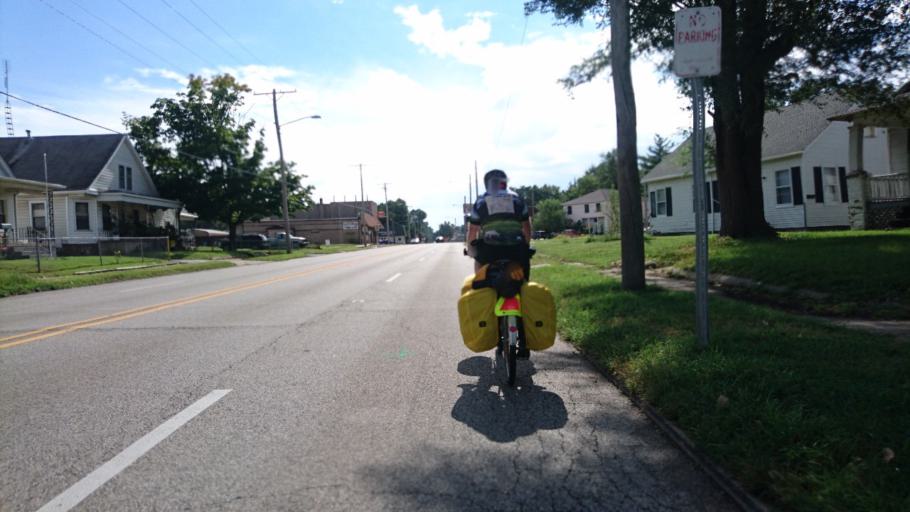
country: US
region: Illinois
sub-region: Sangamon County
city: Grandview
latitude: 39.8280
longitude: -89.6391
